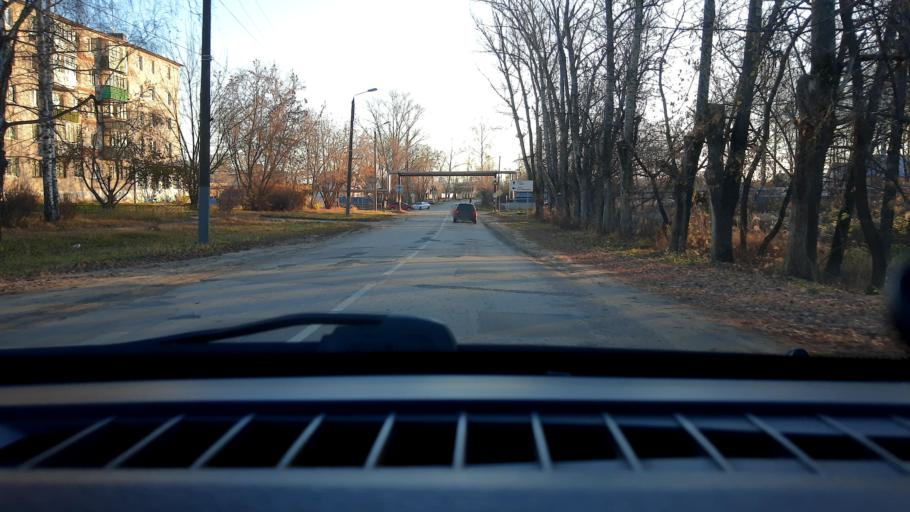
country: RU
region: Nizjnij Novgorod
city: Kstovo
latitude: 56.1812
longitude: 44.1639
